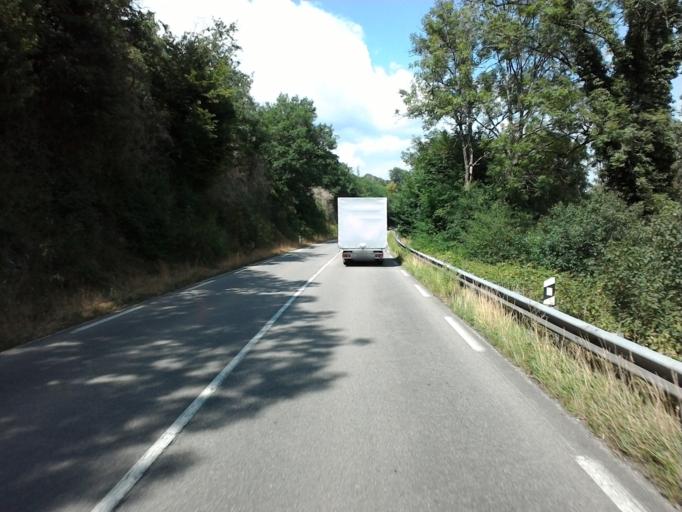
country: FR
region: Franche-Comte
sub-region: Departement du Doubs
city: Montferrand-le-Chateau
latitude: 47.1506
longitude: 5.9375
